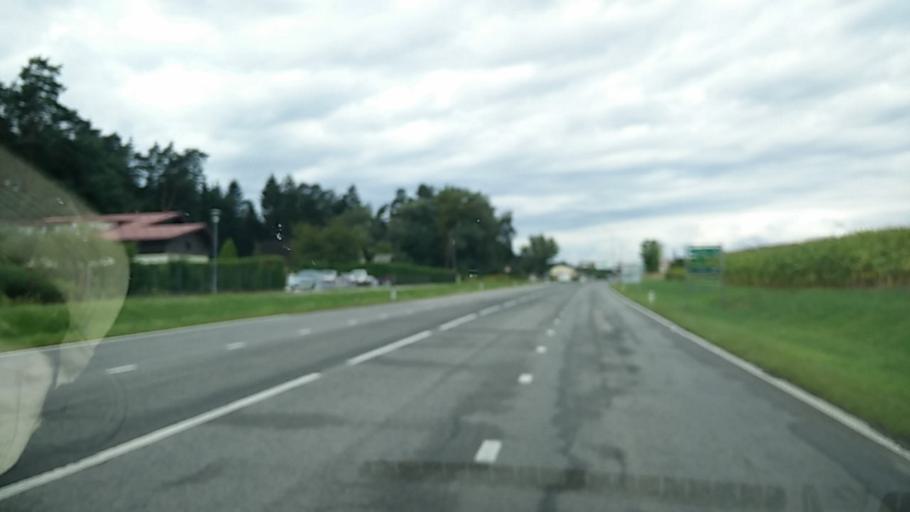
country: AT
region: Carinthia
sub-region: Politischer Bezirk Klagenfurt Land
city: Poggersdorf
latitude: 46.6413
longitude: 14.4544
